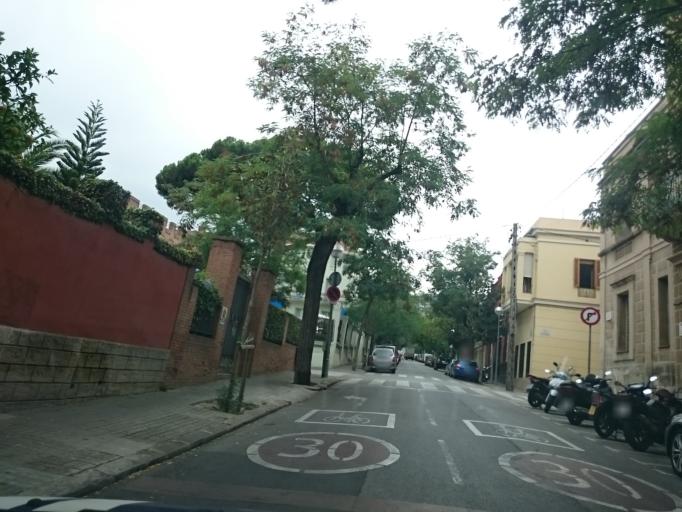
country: ES
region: Catalonia
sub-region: Provincia de Barcelona
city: Sarria-Sant Gervasi
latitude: 41.4035
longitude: 2.1263
